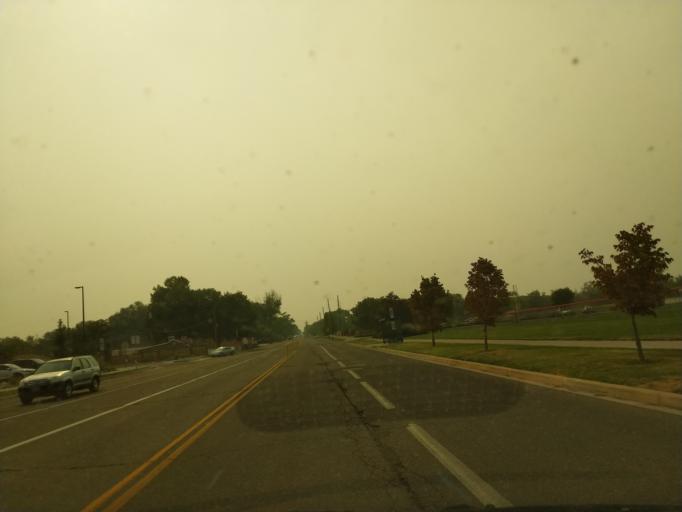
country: US
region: Colorado
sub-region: Mesa County
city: Fruitvale
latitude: 39.0846
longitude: -108.4737
